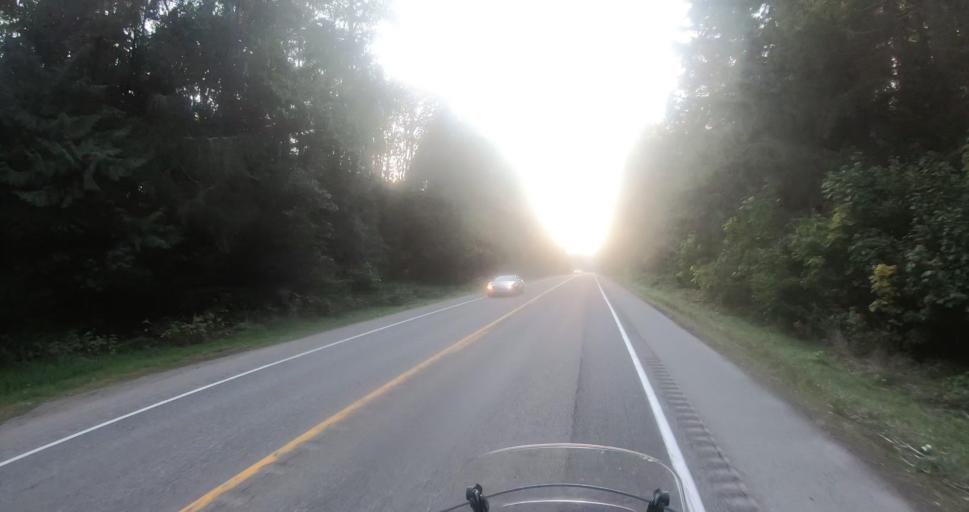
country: US
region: Washington
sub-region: Lewis County
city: Morton
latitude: 46.5387
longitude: -122.0277
